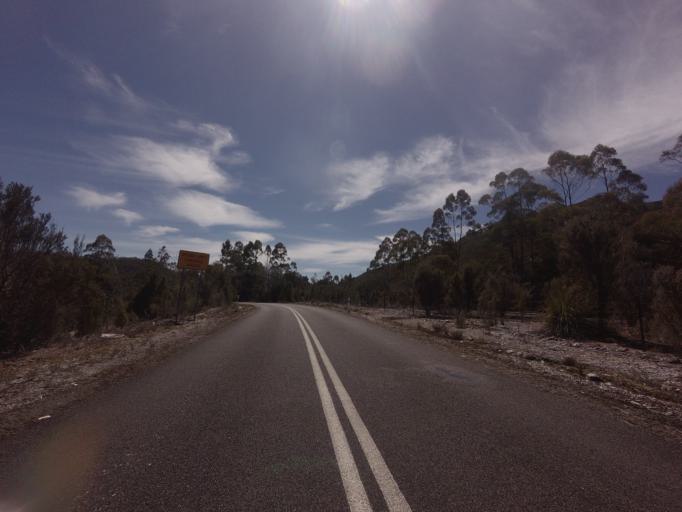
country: AU
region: Tasmania
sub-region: West Coast
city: Queenstown
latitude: -42.7680
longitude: 146.0561
